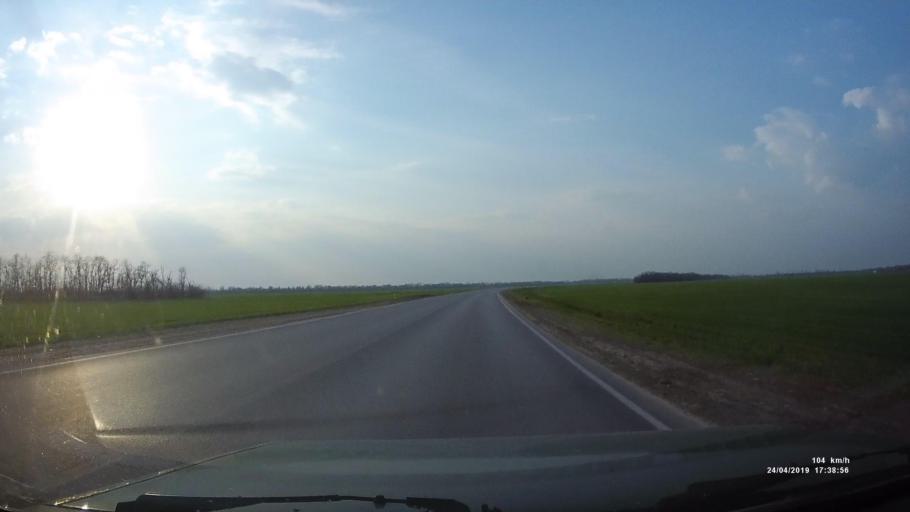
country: RU
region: Rostov
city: Tselina
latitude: 46.5152
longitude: 40.9969
